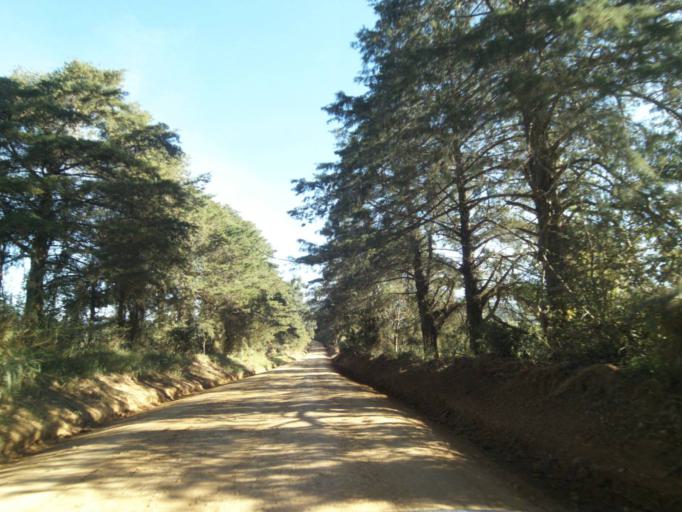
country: BR
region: Parana
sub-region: Tibagi
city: Tibagi
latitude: -24.5292
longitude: -50.5130
